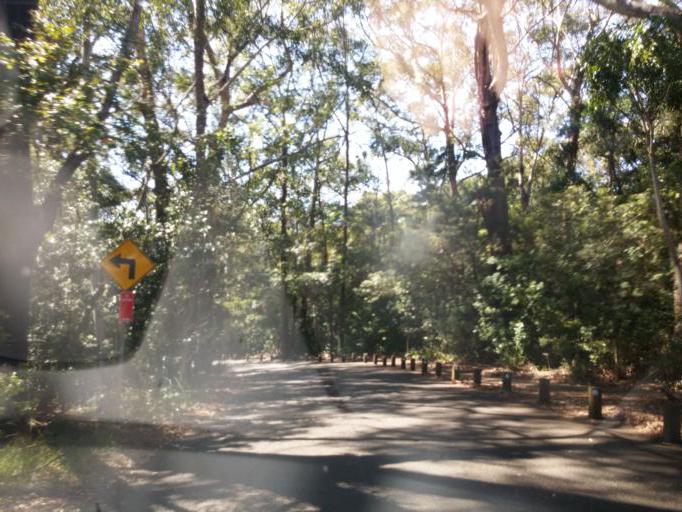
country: AU
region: New South Wales
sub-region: Port Macquarie-Hastings
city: Port Macquarie
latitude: -31.4599
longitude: 152.9296
